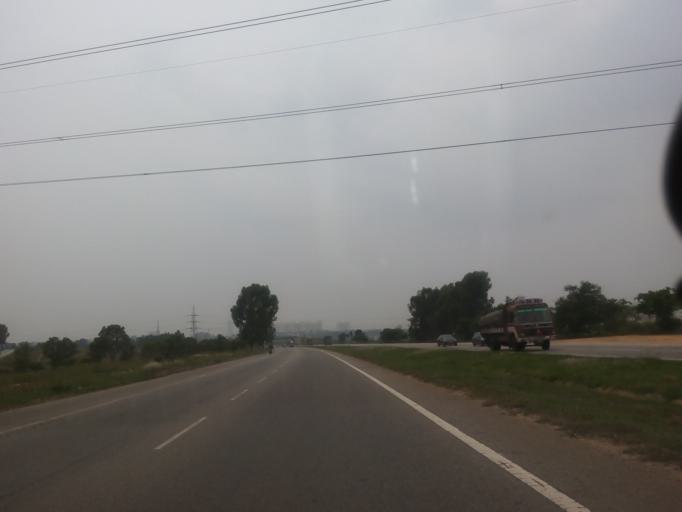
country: IN
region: Karnataka
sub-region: Bangalore Urban
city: Bangalore
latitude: 12.8651
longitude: 77.6427
